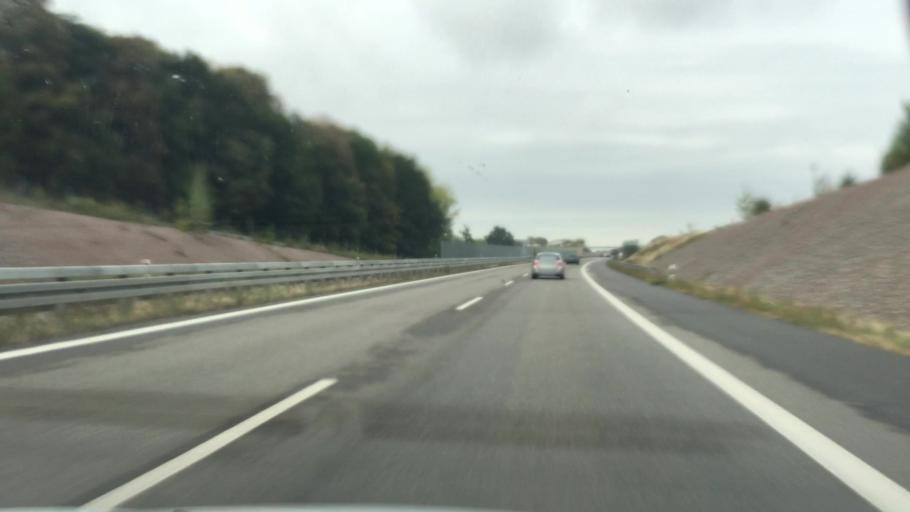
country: DE
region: Saxony
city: Narsdorf
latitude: 51.0174
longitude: 12.6833
